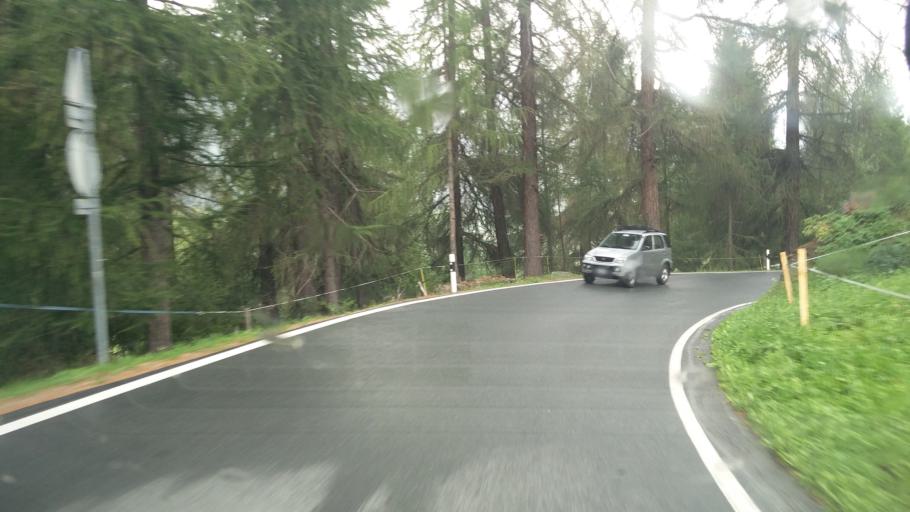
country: IT
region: Trentino-Alto Adige
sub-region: Bolzano
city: Tubre
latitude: 46.5983
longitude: 10.4326
